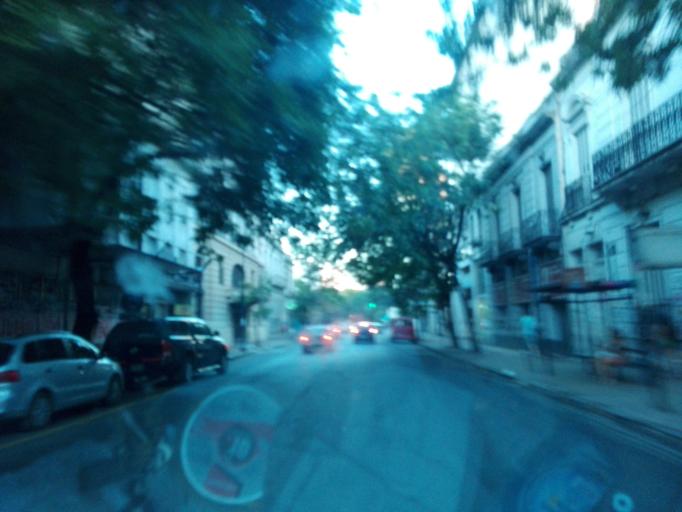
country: AR
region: Buenos Aires
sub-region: Partido de La Plata
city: La Plata
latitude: -34.9175
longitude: -57.9479
